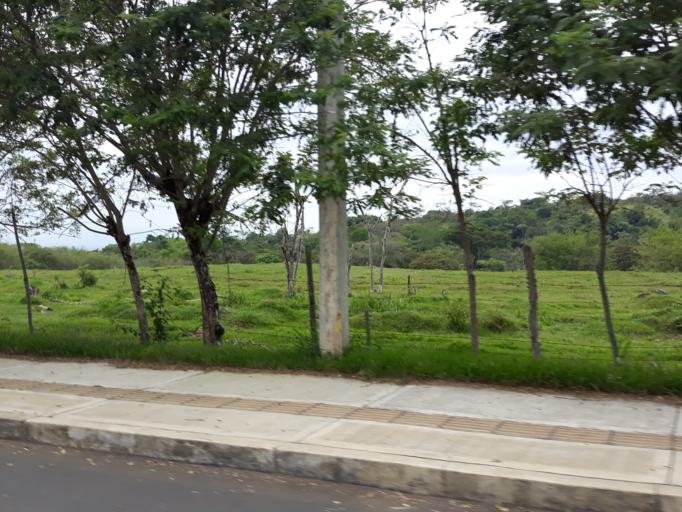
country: CO
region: Valle del Cauca
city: Jamundi
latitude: 3.3475
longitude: -76.5544
